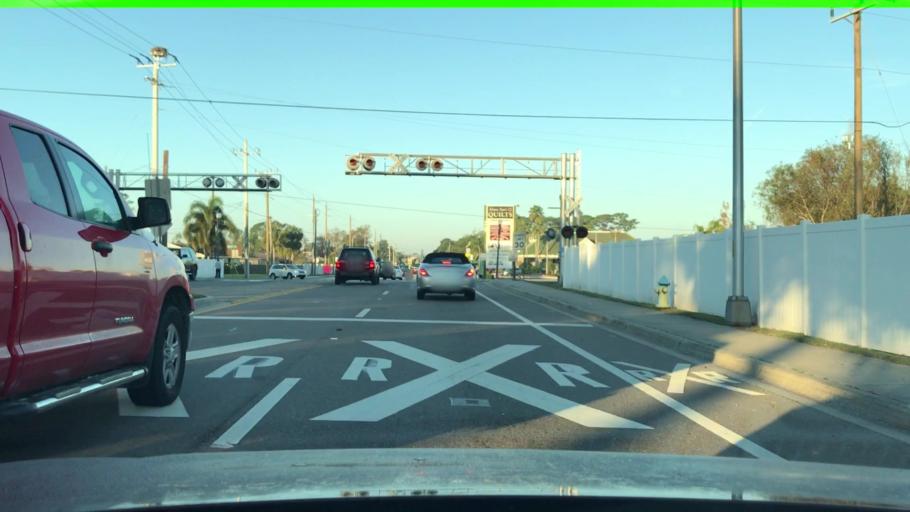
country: US
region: Florida
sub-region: Sarasota County
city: Sarasota Springs
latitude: 27.3230
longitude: -82.4926
